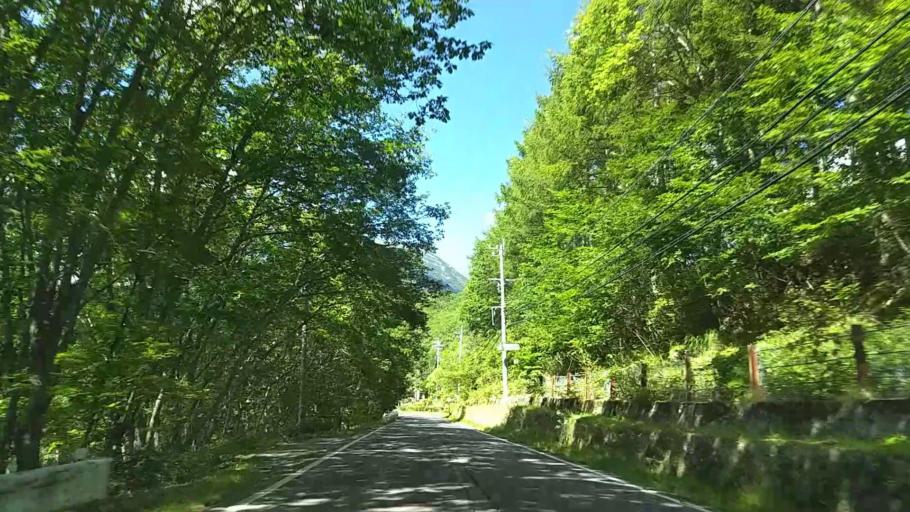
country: JP
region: Nagano
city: Chino
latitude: 36.0693
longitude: 138.2928
